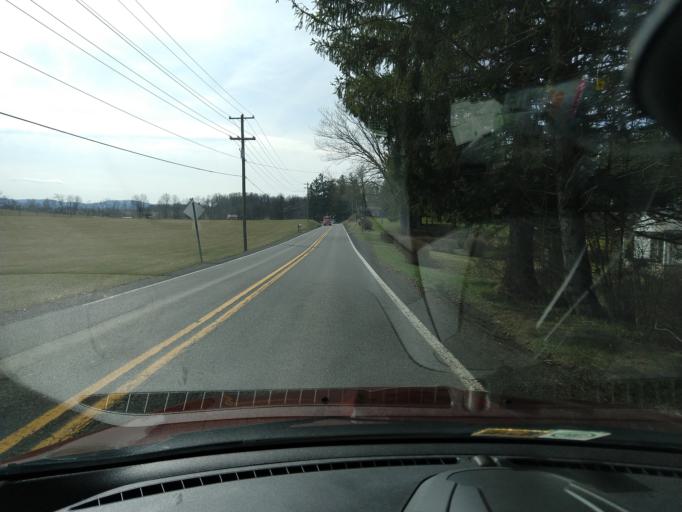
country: US
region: West Virginia
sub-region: Greenbrier County
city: Lewisburg
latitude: 37.8806
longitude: -80.4122
